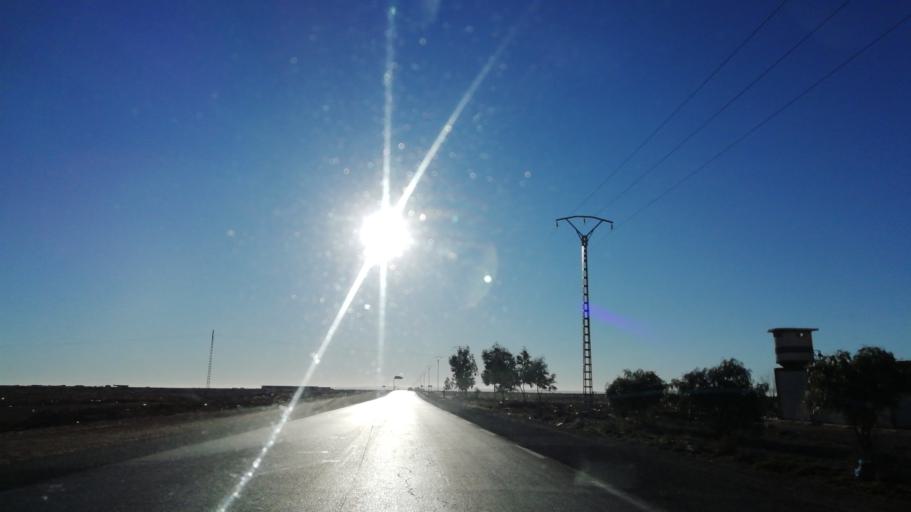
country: DZ
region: Saida
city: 'Ain el Hadjar
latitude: 34.0230
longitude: 0.1011
